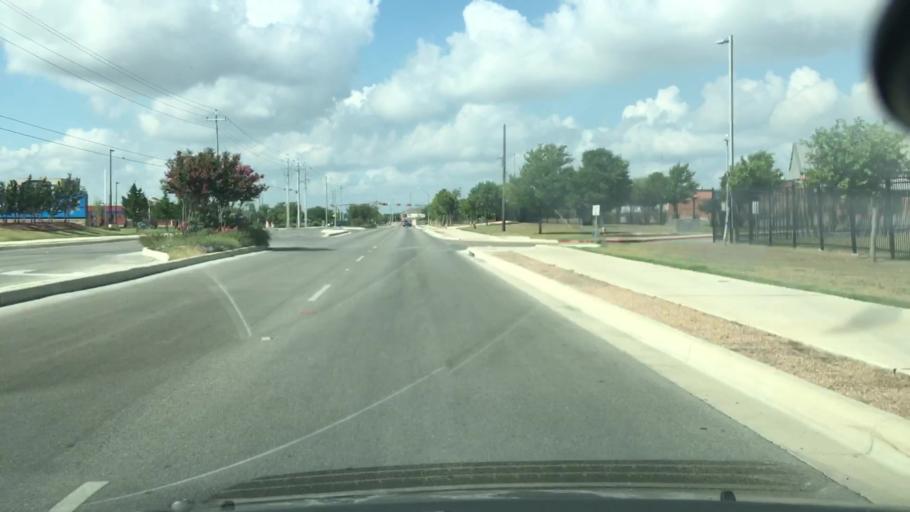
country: US
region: Texas
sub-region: Guadalupe County
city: Cibolo
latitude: 29.5738
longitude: -98.2384
